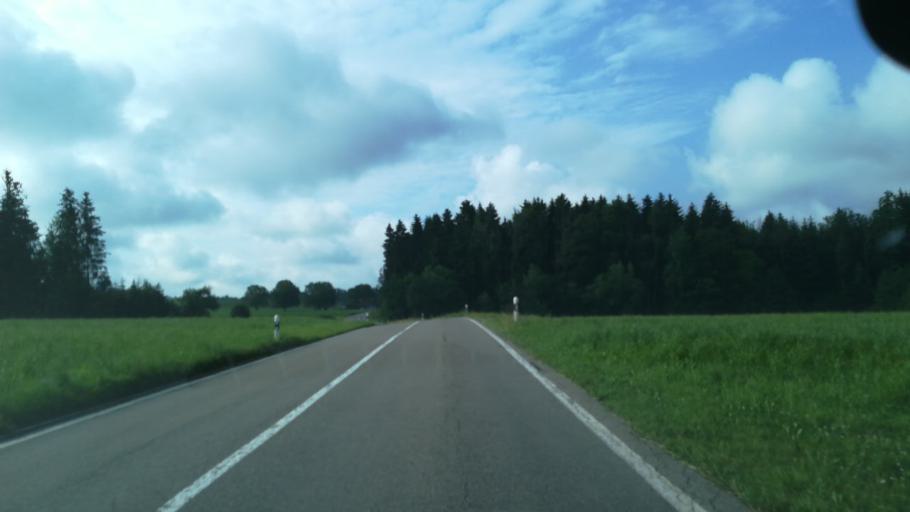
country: CH
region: Saint Gallen
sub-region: Wahlkreis St. Gallen
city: Andwil
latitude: 47.4553
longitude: 9.2521
